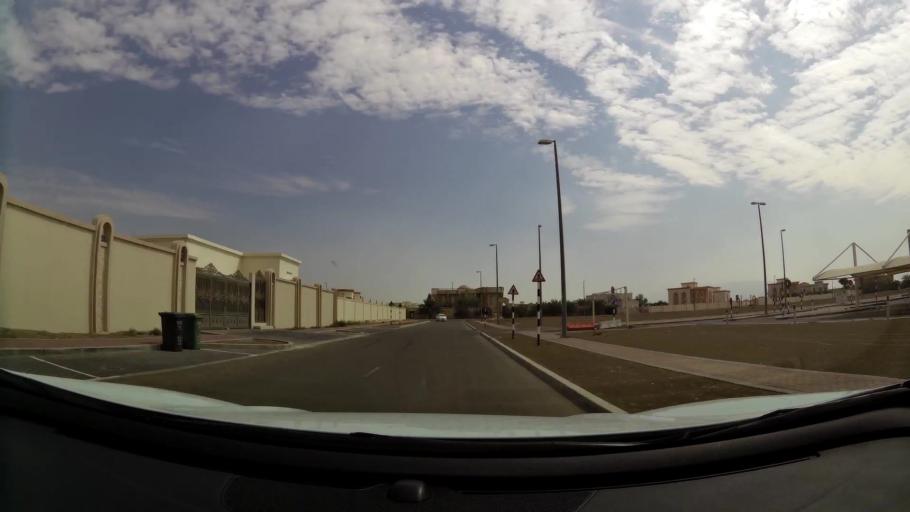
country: AE
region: Abu Dhabi
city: Al Ain
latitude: 24.1890
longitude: 55.7999
